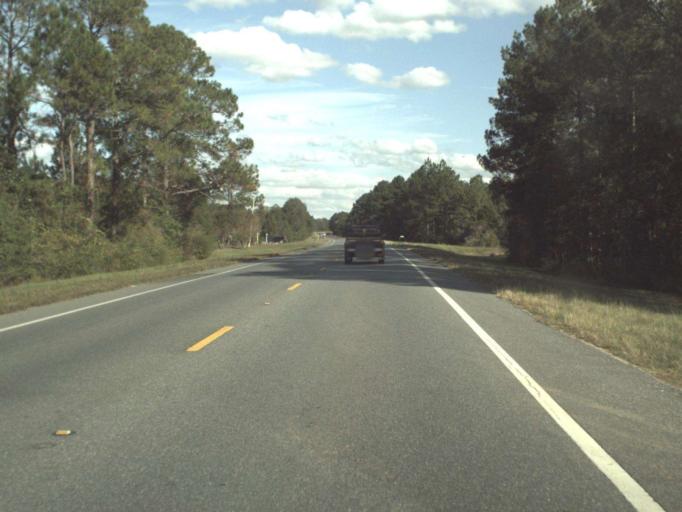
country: US
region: Florida
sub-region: Washington County
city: Chipley
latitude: 30.7777
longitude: -85.6045
